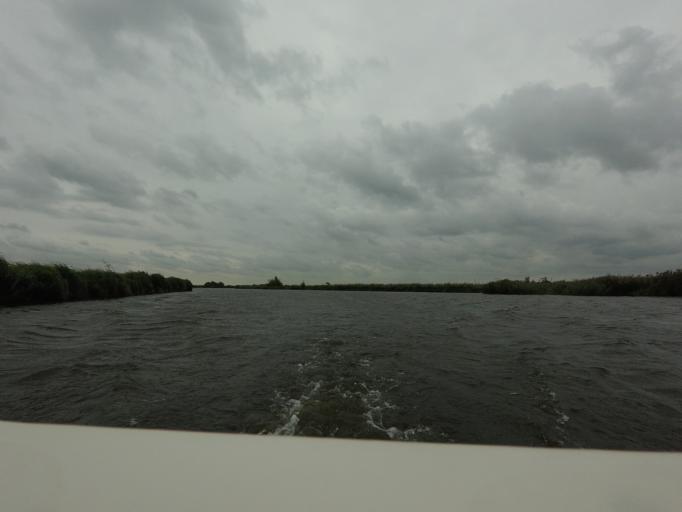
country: NL
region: Friesland
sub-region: Gemeente Boarnsterhim
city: Warten
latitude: 53.1001
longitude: 5.9035
